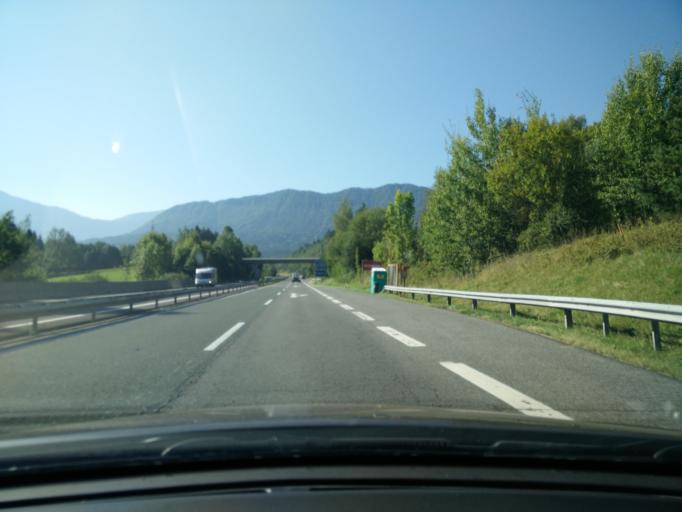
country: AT
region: Carinthia
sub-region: Politischer Bezirk Villach Land
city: Rosegg
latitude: 46.5631
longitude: 14.0063
